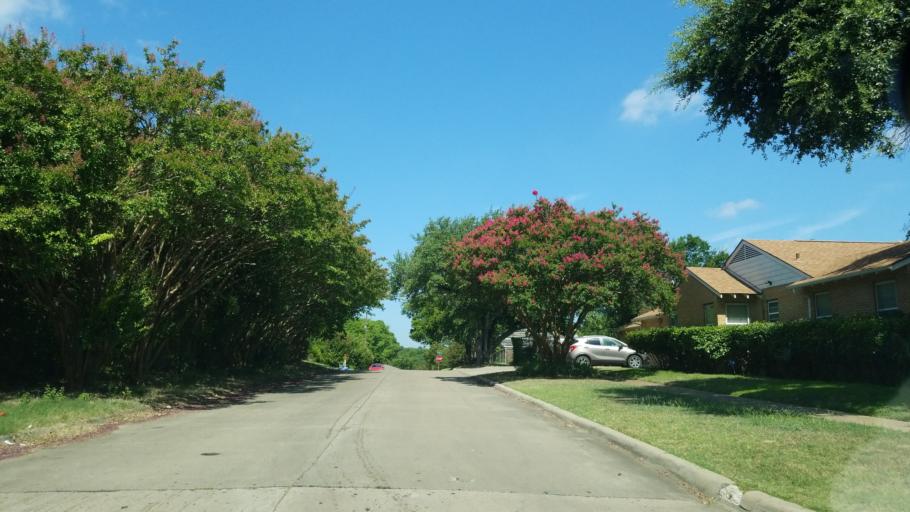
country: US
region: Texas
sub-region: Dallas County
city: Dallas
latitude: 32.7256
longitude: -96.7968
